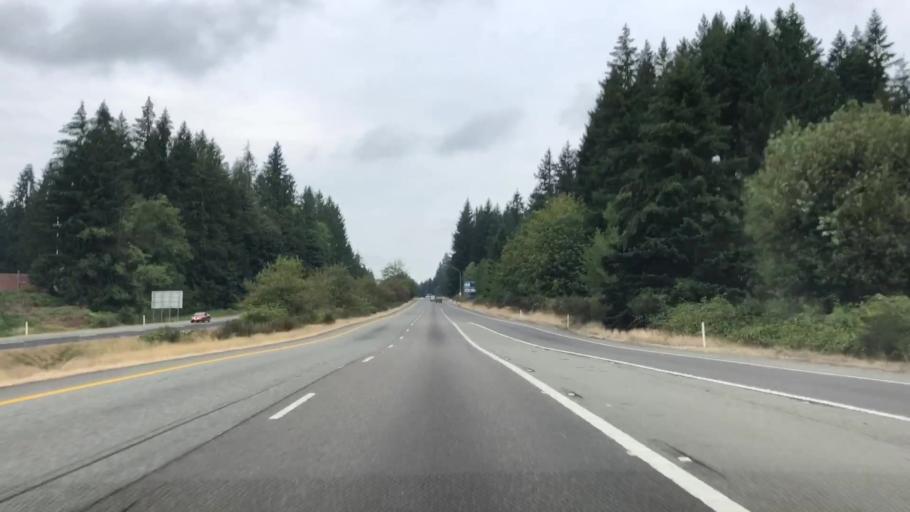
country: US
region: Washington
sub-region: Kitsap County
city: Bethel
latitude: 47.5047
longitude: -122.6478
